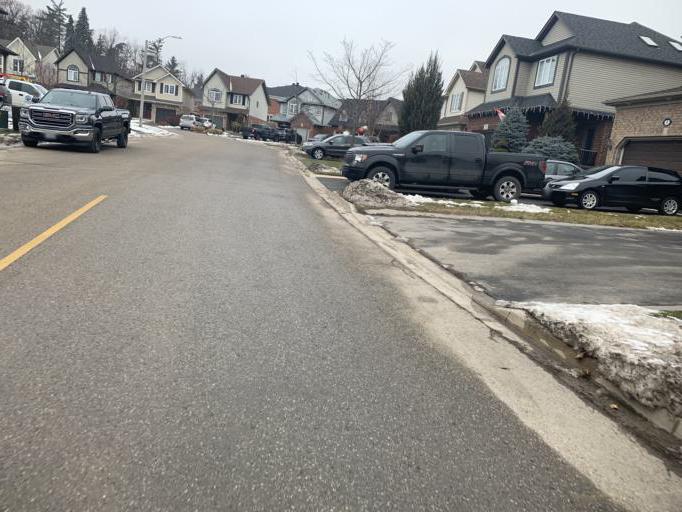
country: CA
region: Ontario
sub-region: Halton
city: Milton
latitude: 43.6613
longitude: -79.9191
